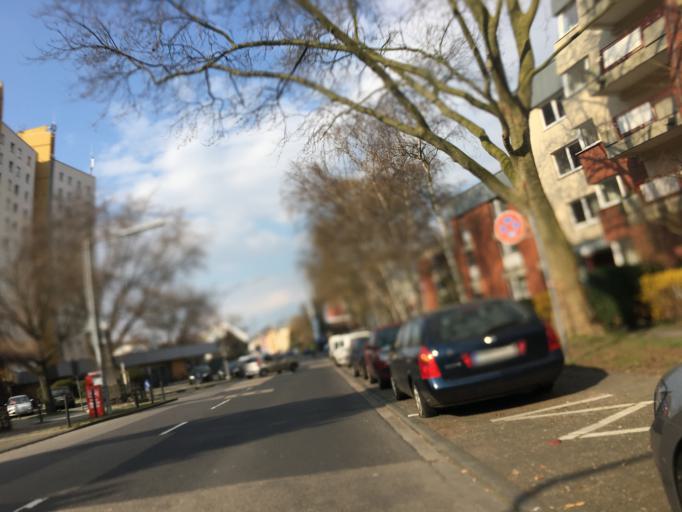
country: DE
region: North Rhine-Westphalia
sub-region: Regierungsbezirk Koln
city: Nippes
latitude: 50.9821
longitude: 6.9444
